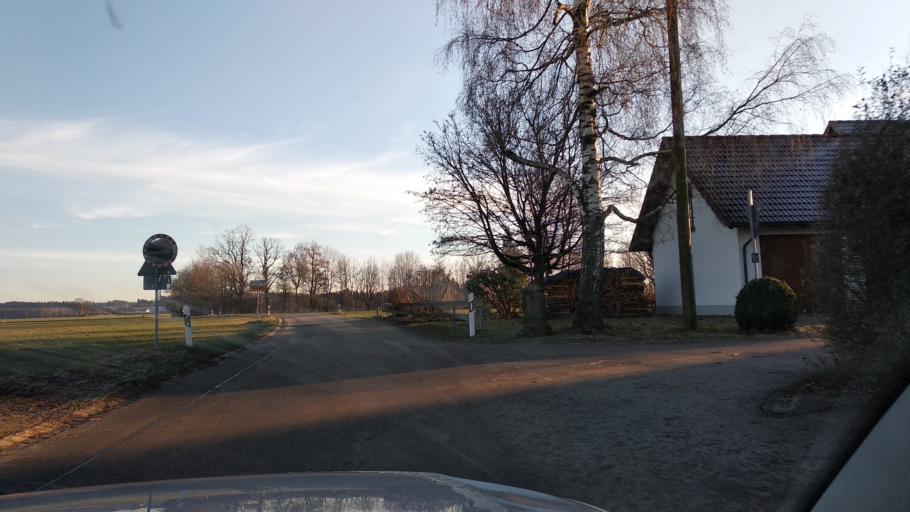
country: DE
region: Bavaria
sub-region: Swabia
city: Lautrach
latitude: 47.9105
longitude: 10.1322
